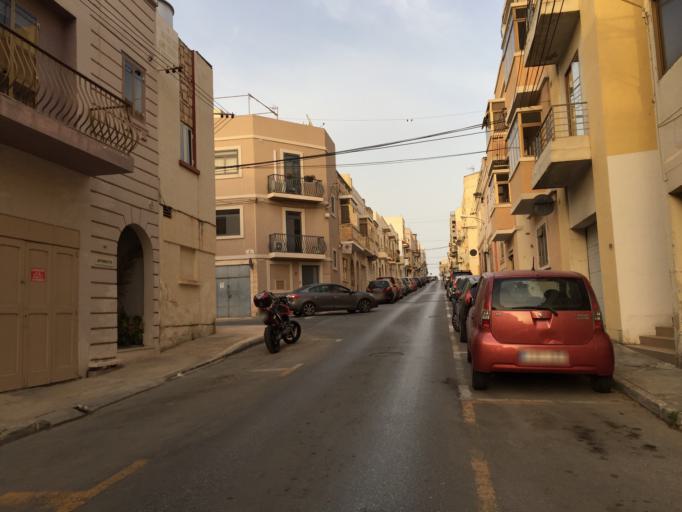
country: MT
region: Il-Fgura
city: Fgura
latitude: 35.8746
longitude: 14.5168
